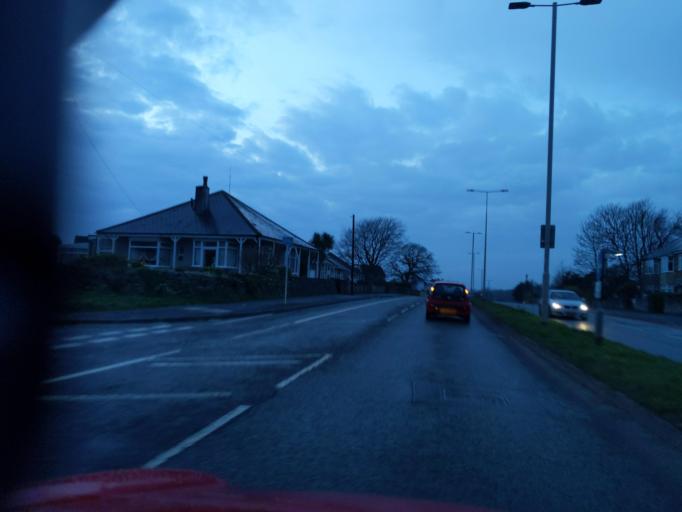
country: GB
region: England
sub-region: Plymouth
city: Plymstock
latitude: 50.3636
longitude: -4.0753
